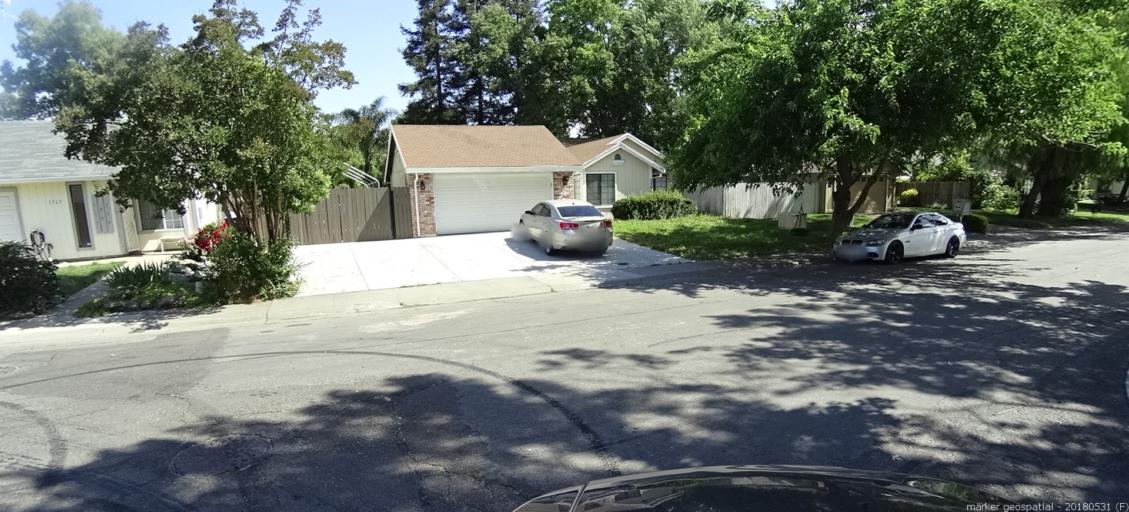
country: US
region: California
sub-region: Sacramento County
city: Sacramento
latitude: 38.6236
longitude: -121.5018
